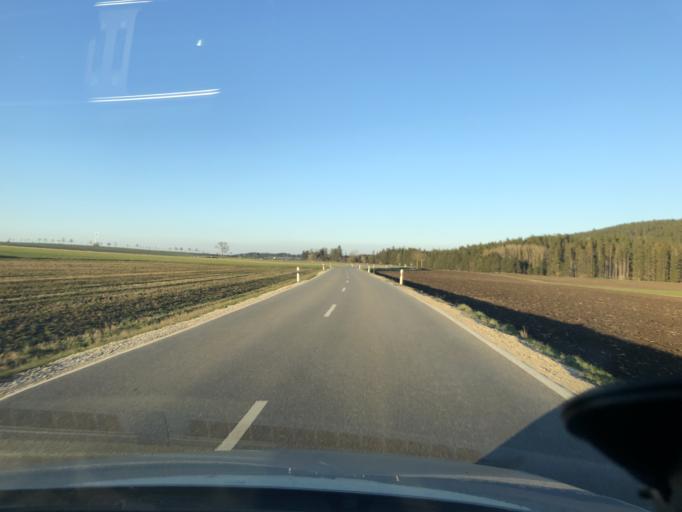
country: DE
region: Baden-Wuerttemberg
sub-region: Freiburg Region
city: Hufingen
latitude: 47.8788
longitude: 8.4692
